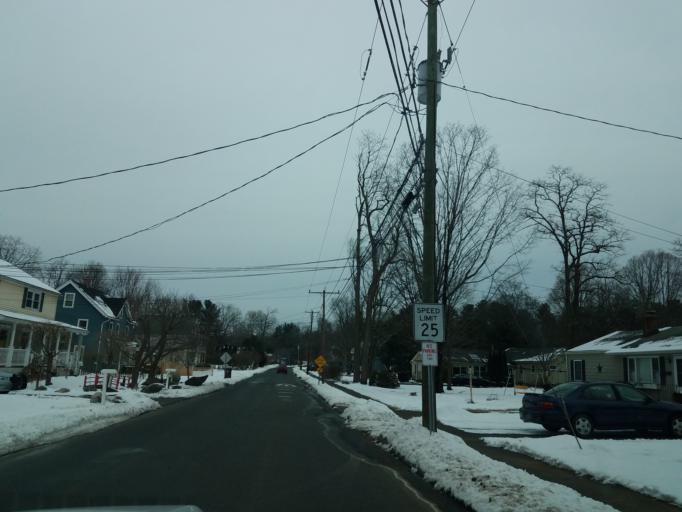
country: US
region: Connecticut
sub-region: Hartford County
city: Collinsville
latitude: 41.7613
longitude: -72.8940
